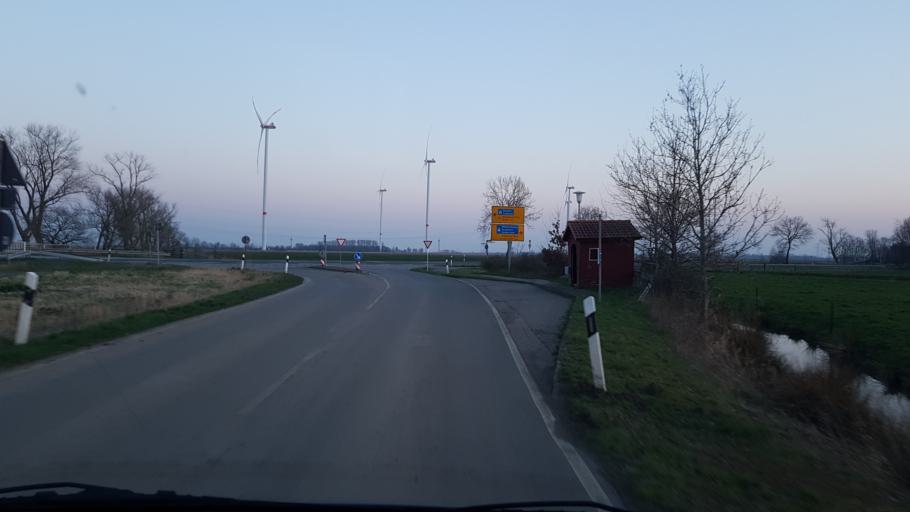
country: DE
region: Lower Saxony
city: Ovelgonne
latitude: 53.2819
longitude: 8.3689
